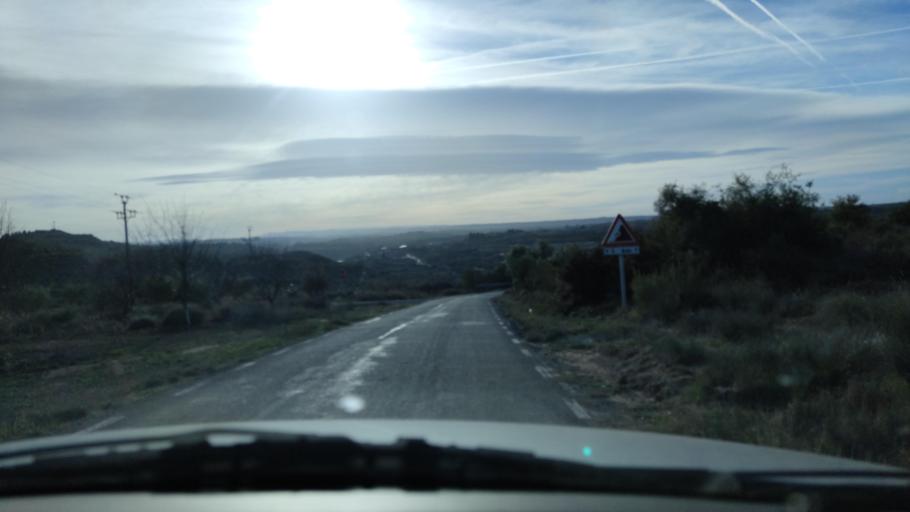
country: ES
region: Catalonia
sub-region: Provincia de Lleida
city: el Cogul
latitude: 41.4766
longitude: 0.6832
